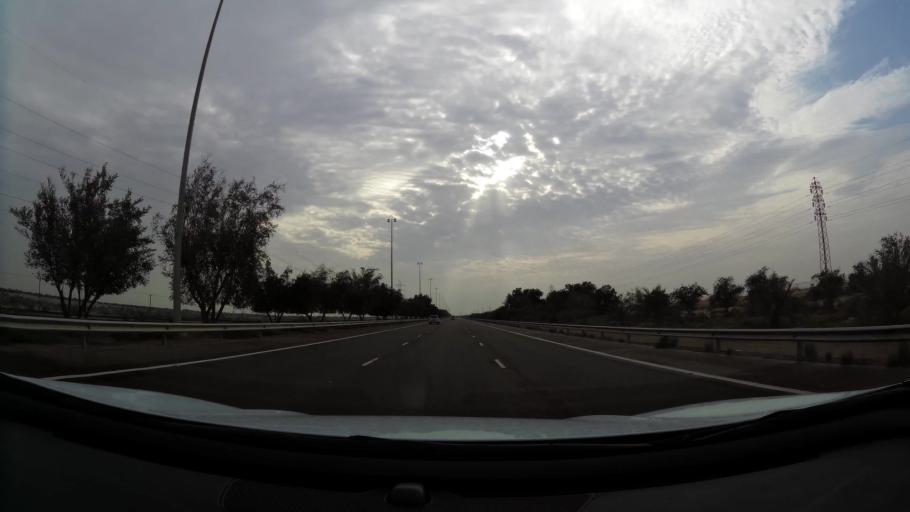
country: AE
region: Abu Dhabi
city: Abu Dhabi
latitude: 24.1995
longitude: 54.9159
